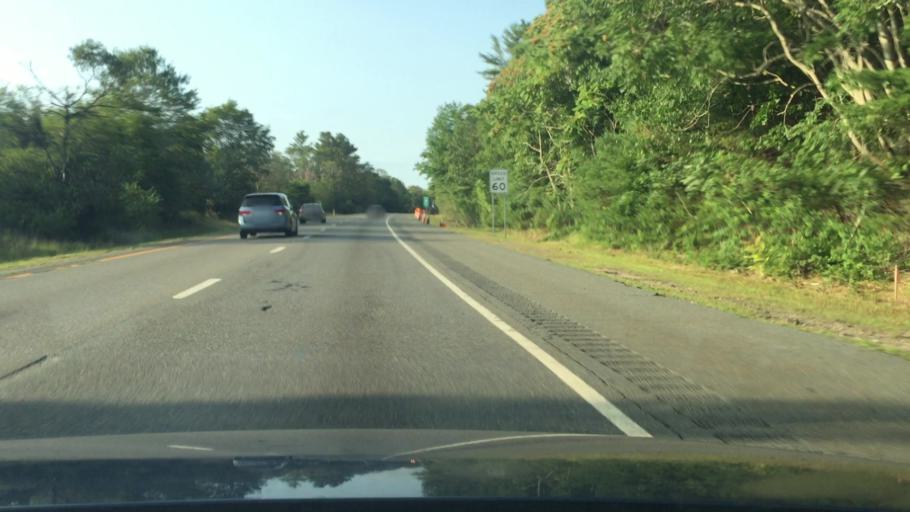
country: US
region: Massachusetts
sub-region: Plymouth County
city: Marshfield
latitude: 42.0489
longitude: -70.7238
